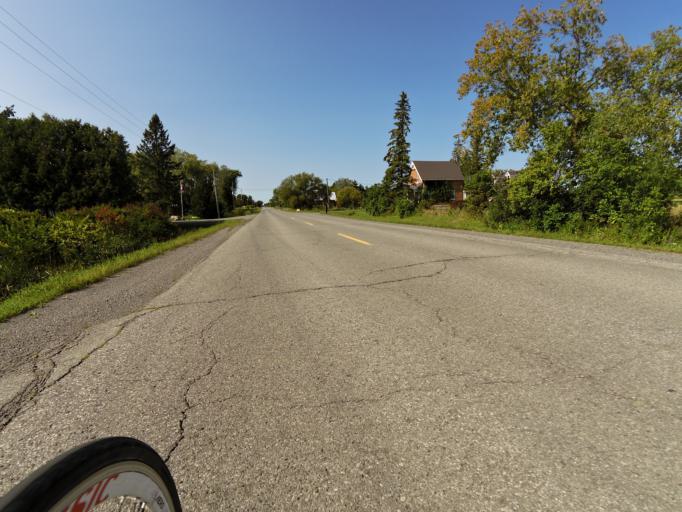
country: CA
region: Ontario
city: Carleton Place
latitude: 45.3365
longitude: -76.0958
